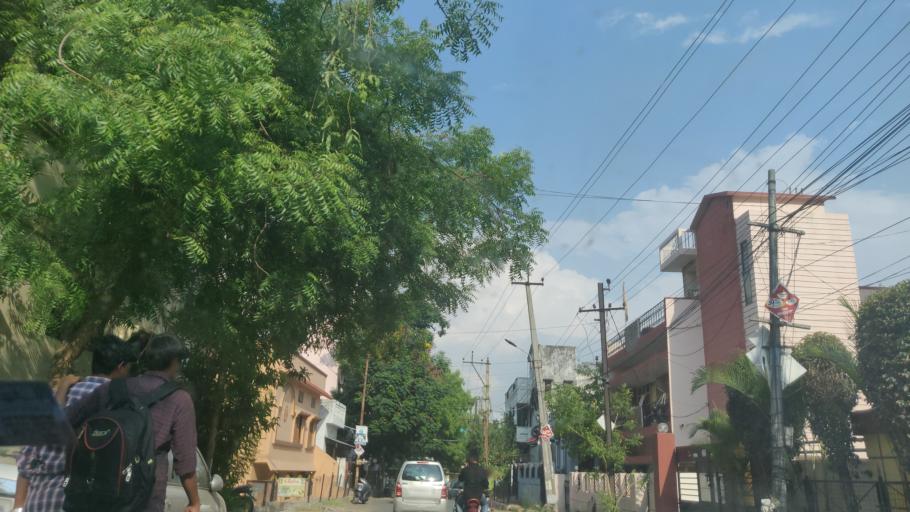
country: IN
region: Telangana
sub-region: Rangareddi
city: Gaddi Annaram
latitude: 17.3757
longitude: 78.5186
